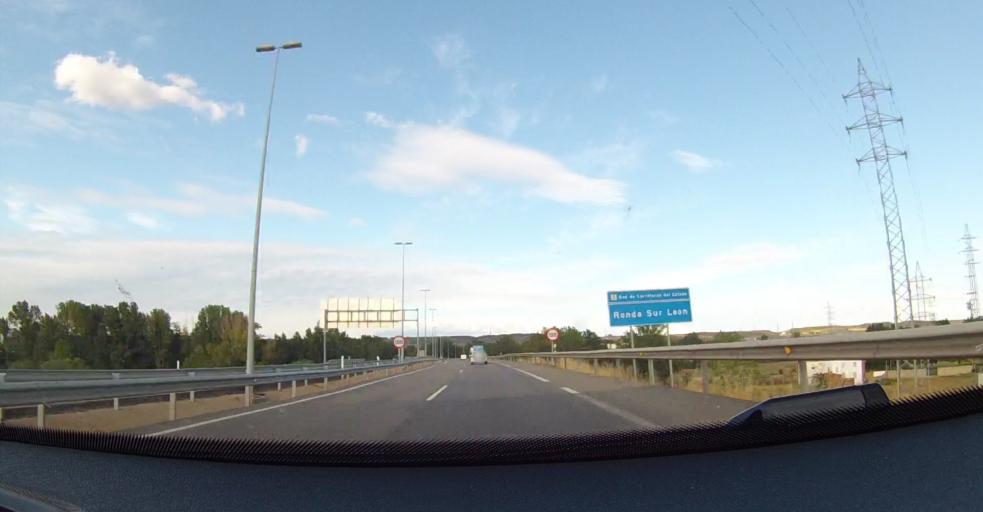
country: ES
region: Castille and Leon
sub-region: Provincia de Leon
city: Leon
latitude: 42.5707
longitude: -5.5778
